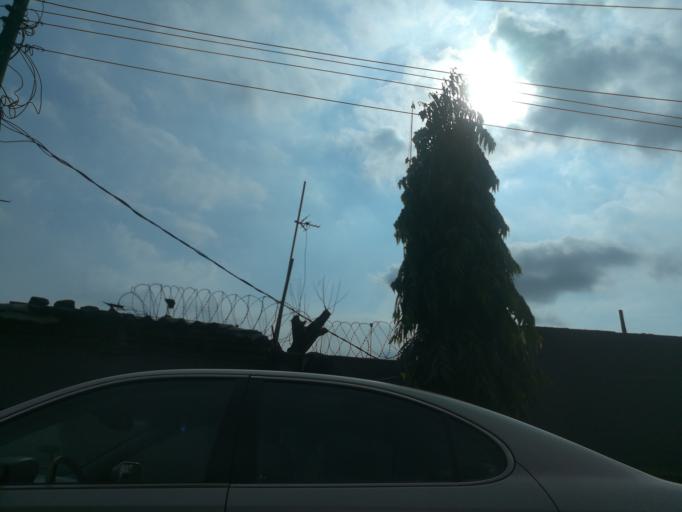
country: NG
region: Lagos
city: Oshodi
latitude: 6.5752
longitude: 3.3561
